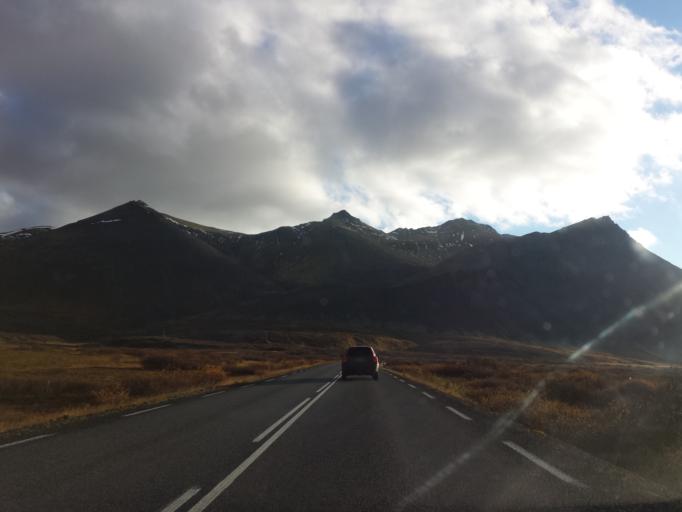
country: IS
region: West
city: Borgarnes
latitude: 64.5214
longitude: -21.8864
